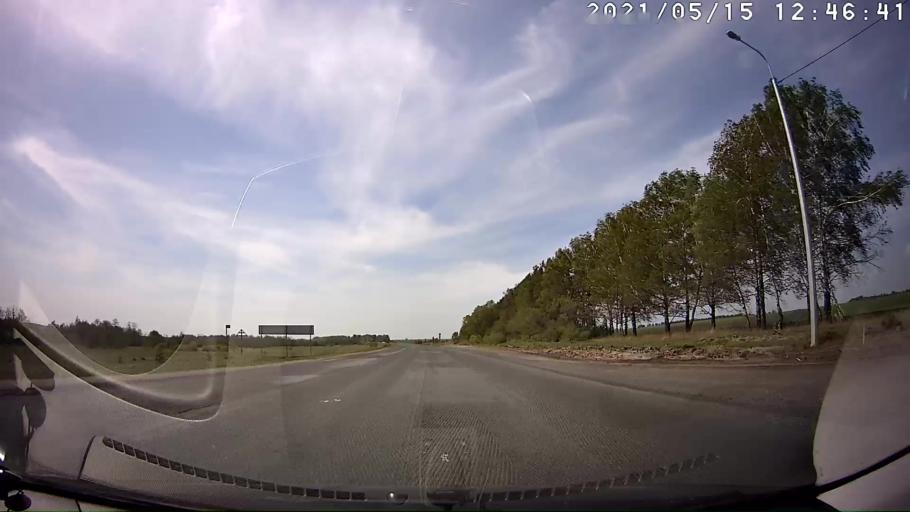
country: RU
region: Mariy-El
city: Sovetskiy
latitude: 56.7478
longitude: 48.3338
